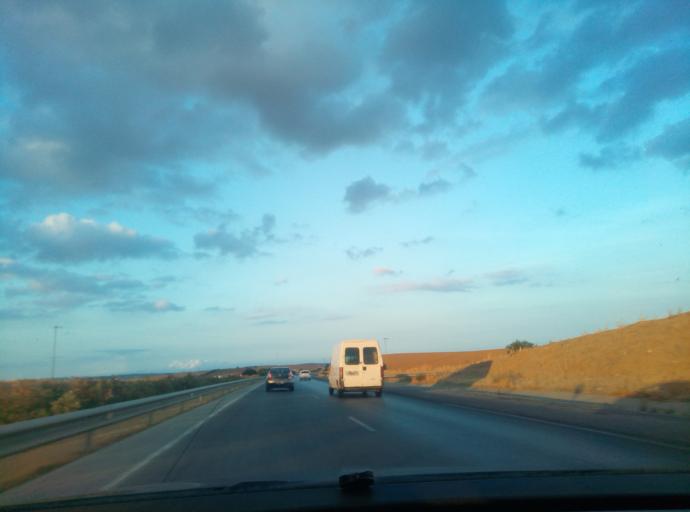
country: TN
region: Tunis
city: Oued Lill
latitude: 36.7213
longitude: 9.9856
